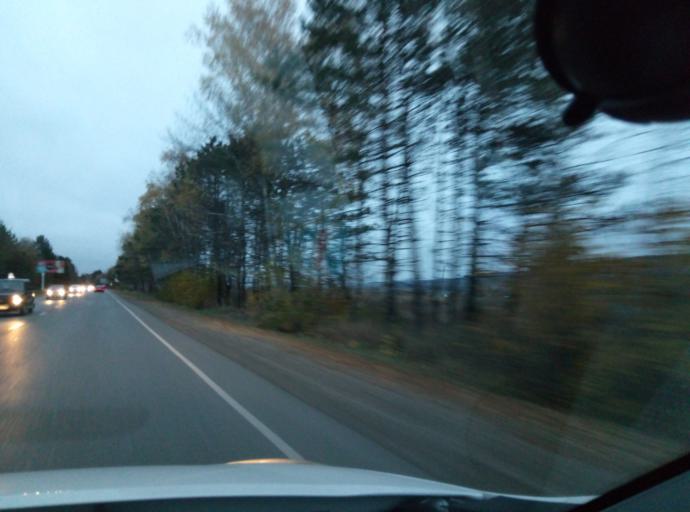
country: RU
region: Stavropol'skiy
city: Vinsady
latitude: 44.0546
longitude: 42.9284
